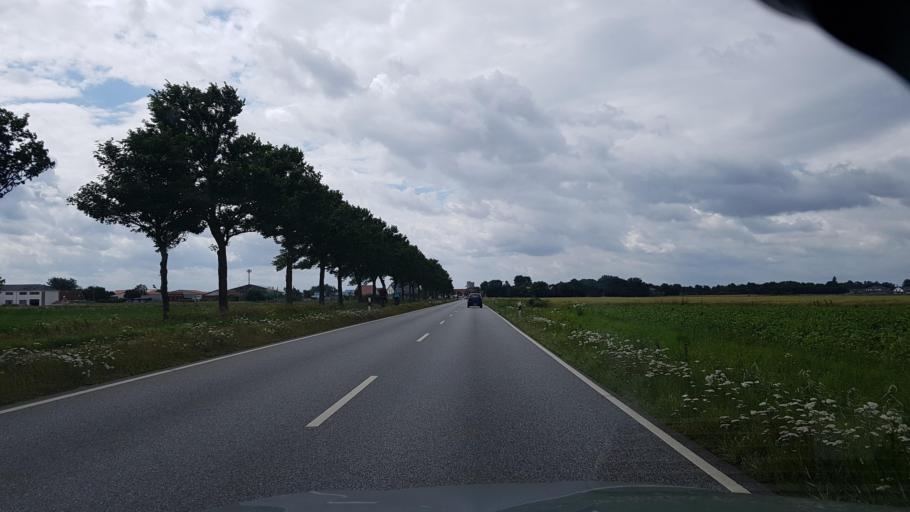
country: DE
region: Schleswig-Holstein
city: Oesterdeichstrich
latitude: 54.1434
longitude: 8.8761
